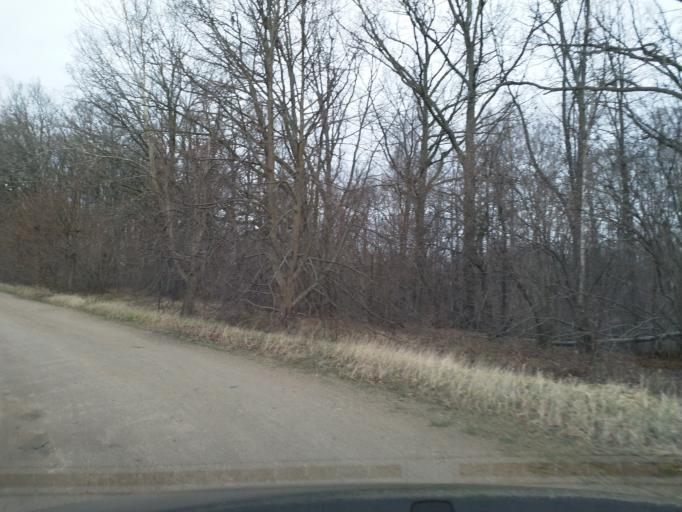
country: LV
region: Kuldigas Rajons
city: Kuldiga
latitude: 56.9486
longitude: 22.0068
